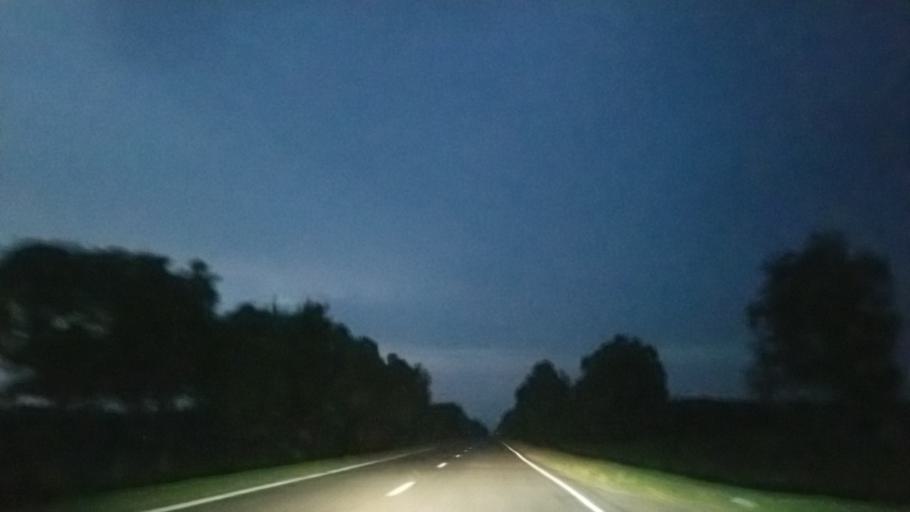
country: PL
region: Lublin Voivodeship
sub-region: Powiat bialski
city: Koden
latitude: 51.8909
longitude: 23.6504
